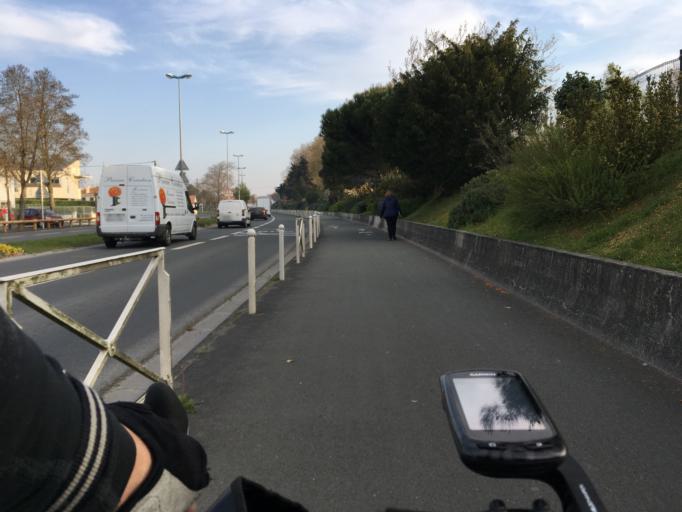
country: FR
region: Poitou-Charentes
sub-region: Departement de la Charente-Maritime
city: La Rochelle
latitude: 46.1748
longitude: -1.1503
